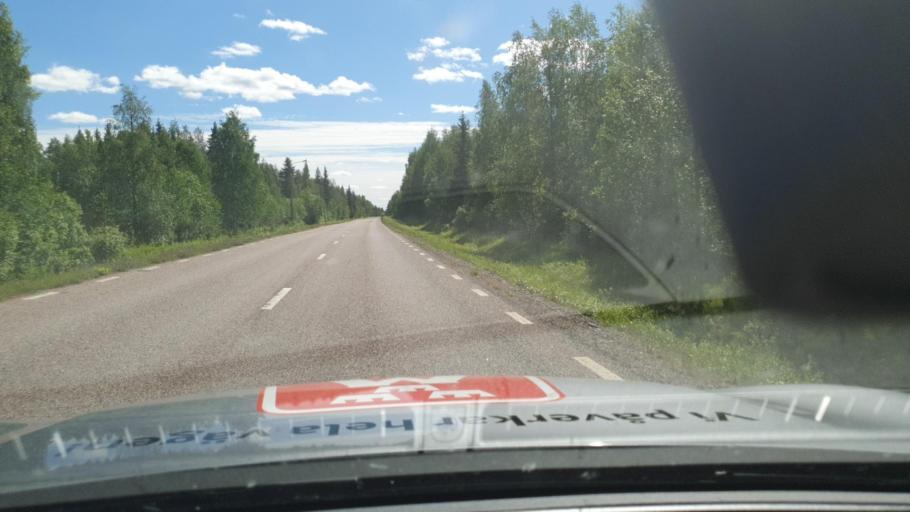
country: FI
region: Lapland
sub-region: Tunturi-Lappi
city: Kolari
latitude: 67.0958
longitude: 23.6553
